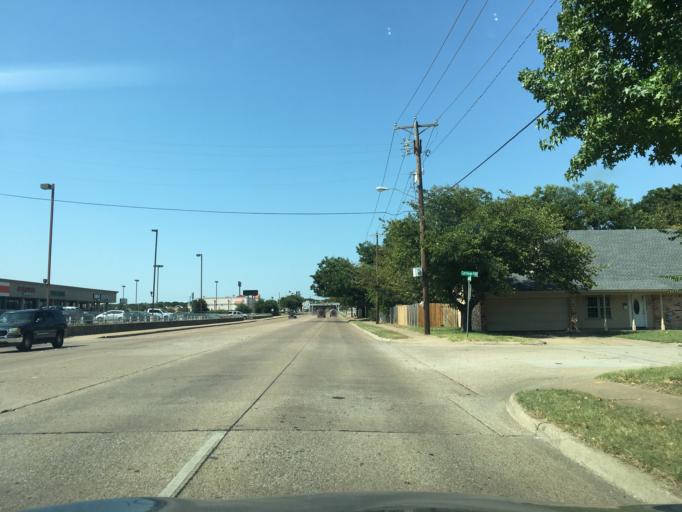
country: US
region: Texas
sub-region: Tarrant County
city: Forest Hill
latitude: 32.6567
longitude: -97.2698
